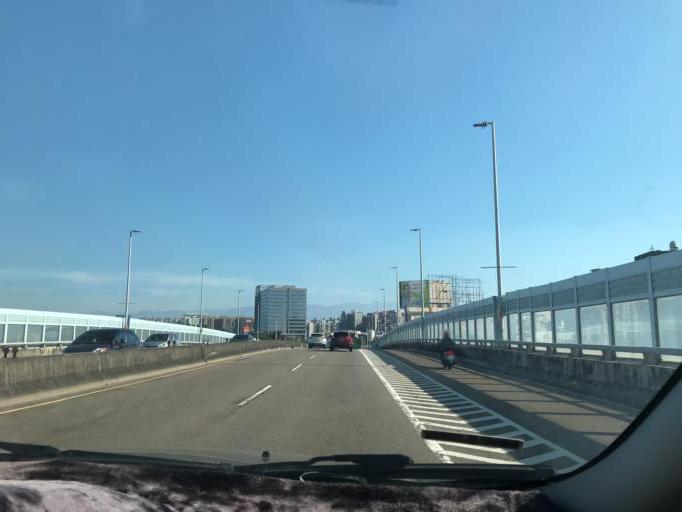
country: TW
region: Taiwan
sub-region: Hsinchu
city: Hsinchu
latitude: 24.8093
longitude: 120.9871
